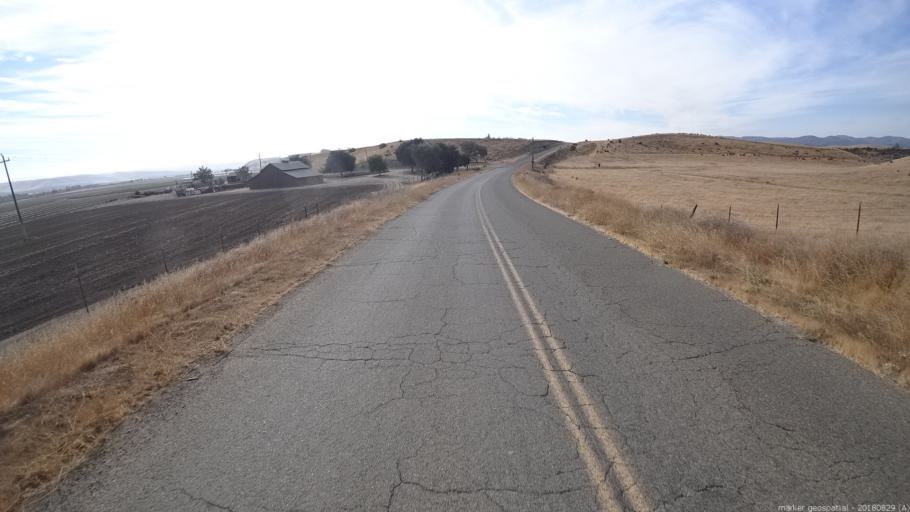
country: US
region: California
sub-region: Monterey County
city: King City
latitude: 36.0909
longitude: -121.0092
